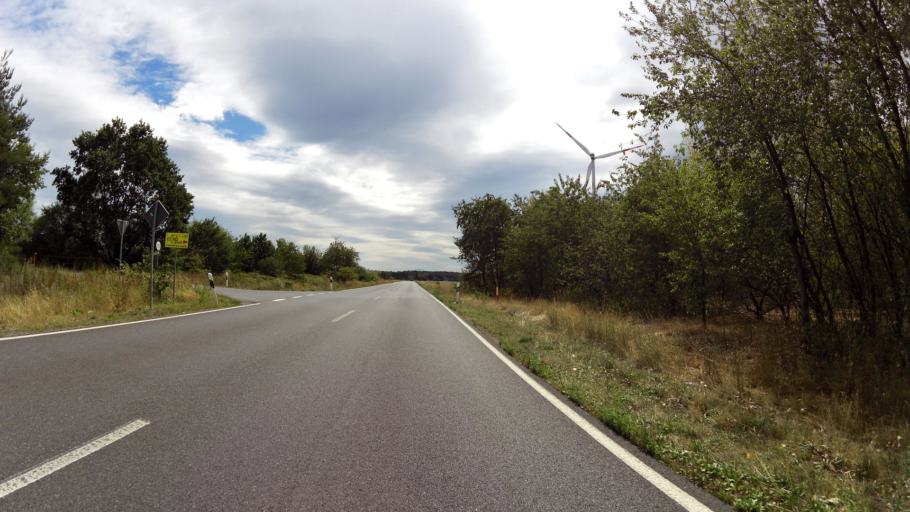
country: DE
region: Brandenburg
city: Heinersbruck
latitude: 51.7841
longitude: 14.4727
